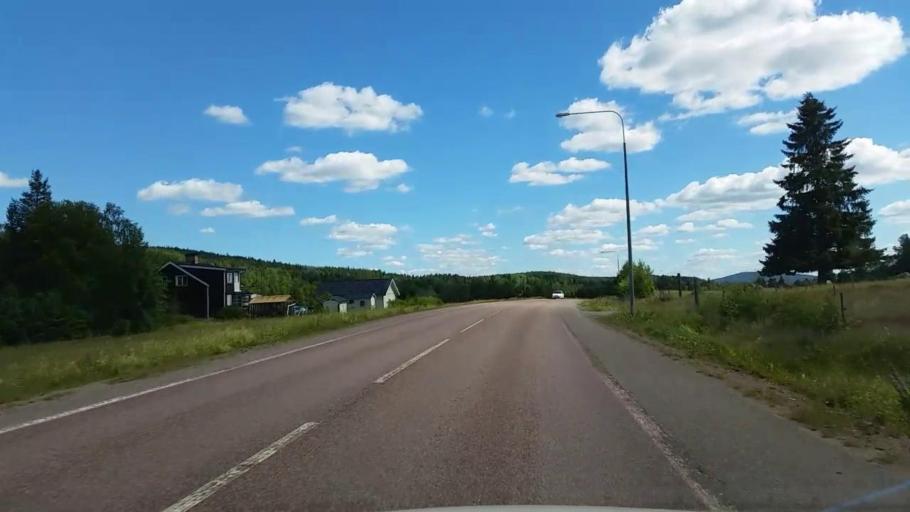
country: SE
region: Dalarna
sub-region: Faluns Kommun
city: Svardsjo
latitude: 60.8478
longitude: 15.7573
